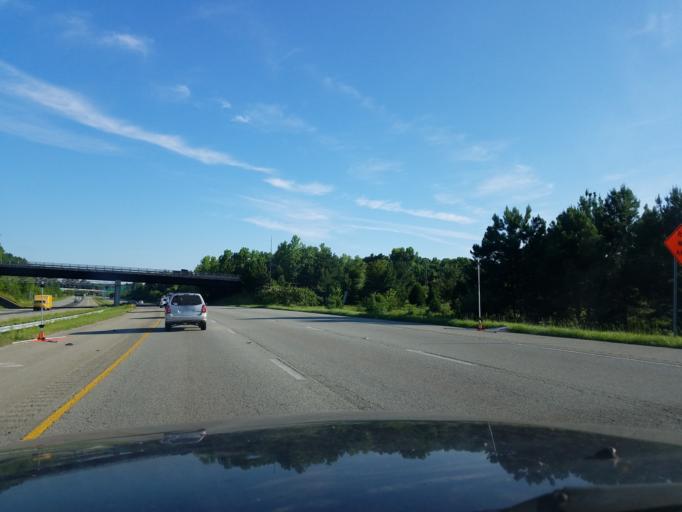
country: US
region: North Carolina
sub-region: Durham County
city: Durham
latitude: 36.0040
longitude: -78.8637
